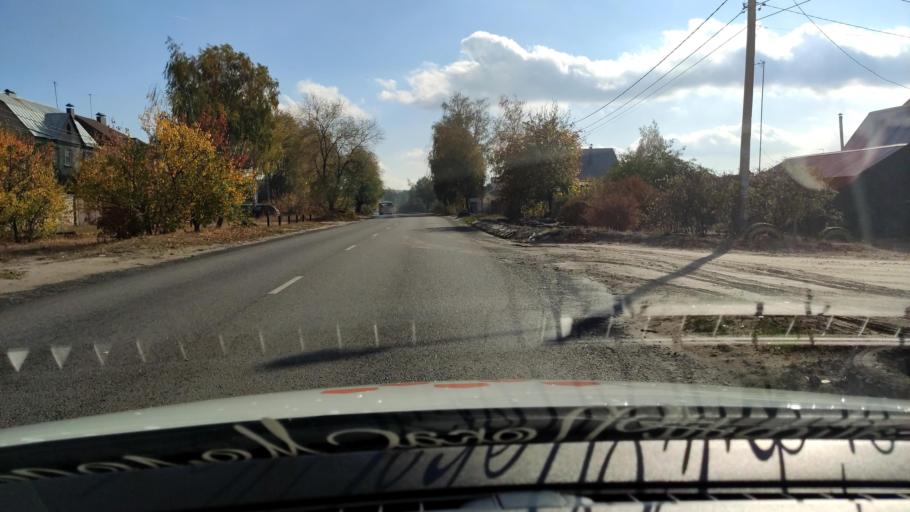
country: RU
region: Voronezj
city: Pridonskoy
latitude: 51.6821
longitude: 39.0726
